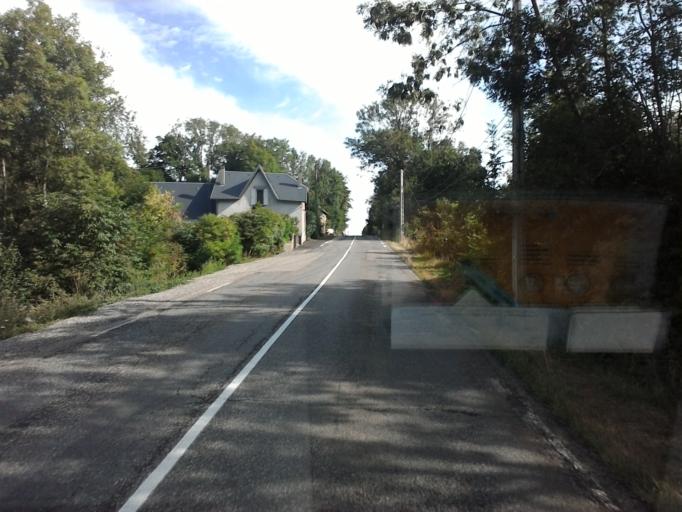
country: FR
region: Rhone-Alpes
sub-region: Departement de l'Isere
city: Pierre-Chatel
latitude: 44.9951
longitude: 5.7731
